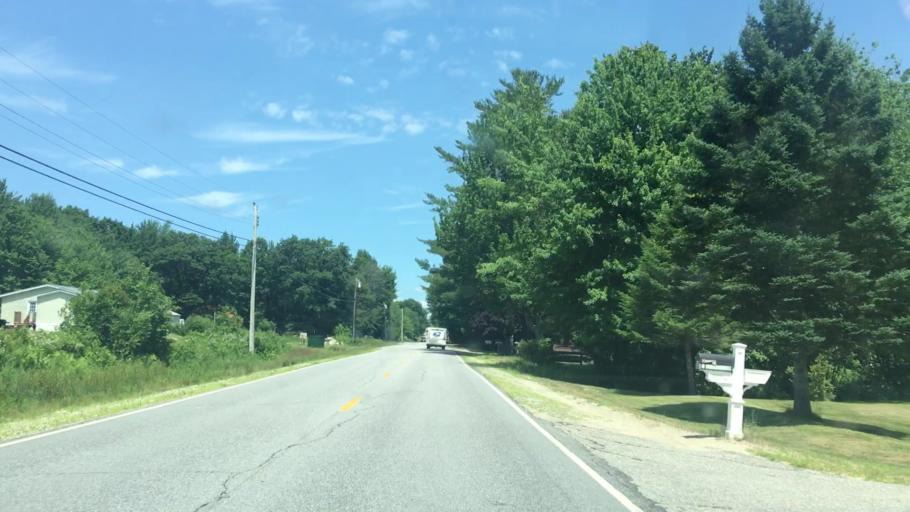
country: US
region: Maine
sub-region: Androscoggin County
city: Livermore
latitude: 44.3609
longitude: -70.2049
